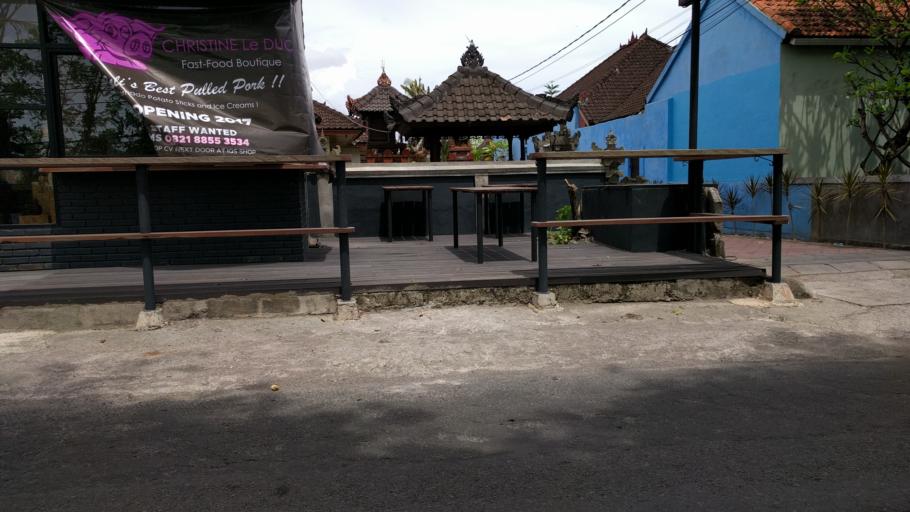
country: ID
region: Bali
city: Banjar Gunungpande
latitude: -8.6523
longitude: 115.1489
